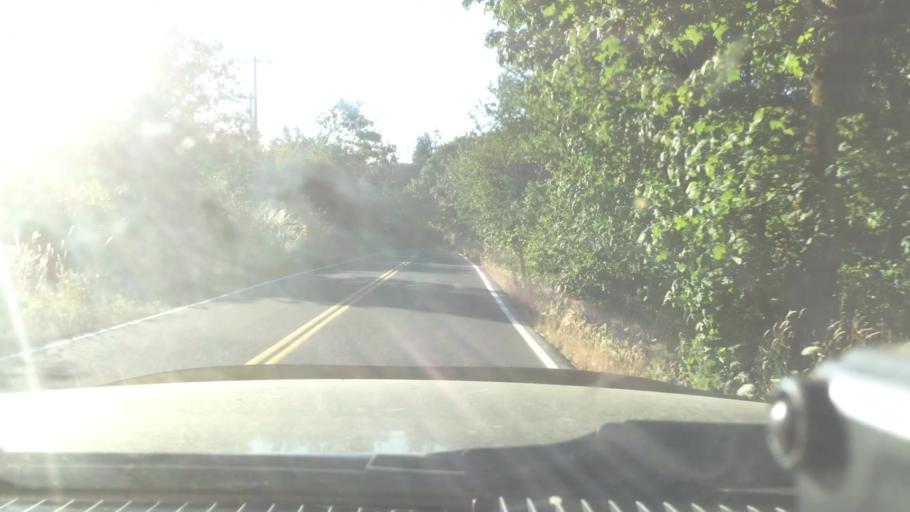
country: US
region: Oregon
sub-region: Yamhill County
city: Newberg
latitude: 45.3357
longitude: -122.9376
